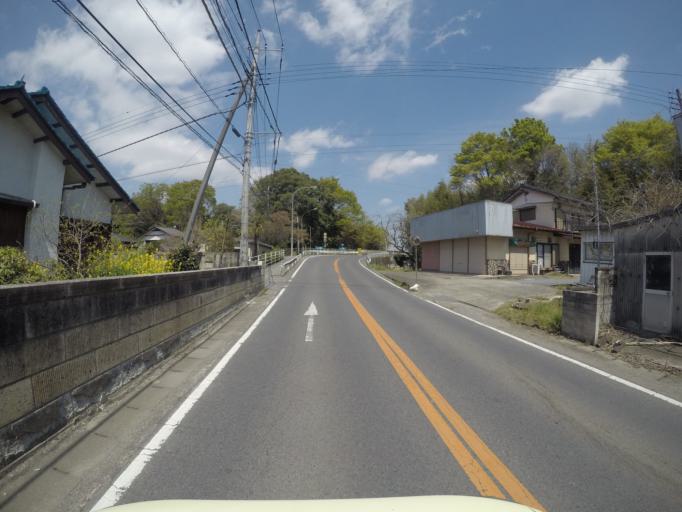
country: JP
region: Tochigi
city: Mibu
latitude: 36.4154
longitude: 139.7864
